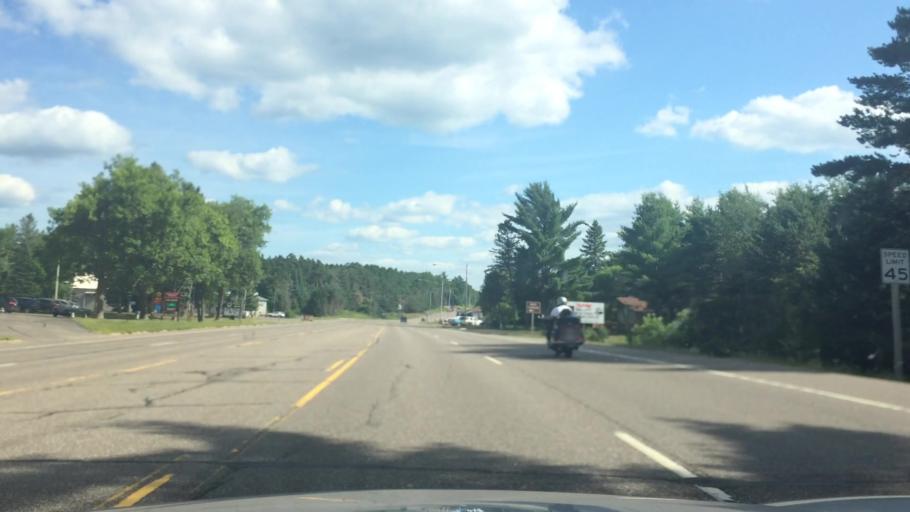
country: US
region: Wisconsin
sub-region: Vilas County
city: Lac du Flambeau
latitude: 45.8076
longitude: -89.7249
